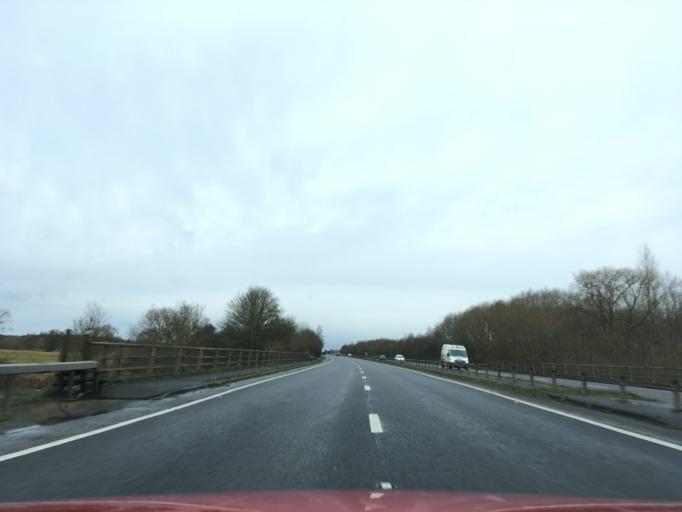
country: GB
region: England
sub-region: Warwickshire
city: Alcester
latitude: 52.1910
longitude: -1.8766
